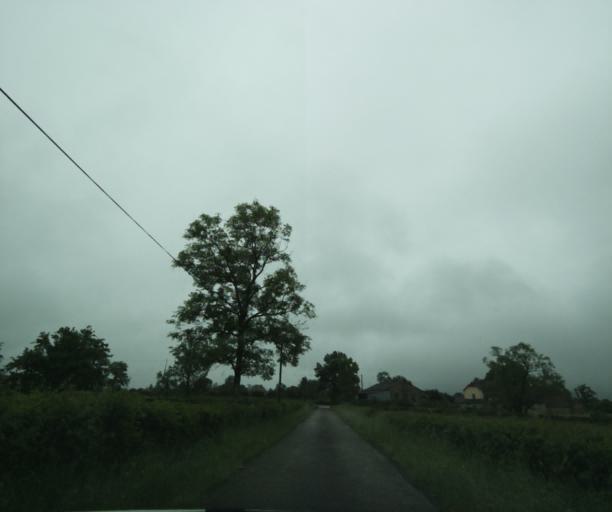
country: FR
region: Bourgogne
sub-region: Departement de Saone-et-Loire
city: Charolles
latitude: 46.3878
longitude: 4.3249
